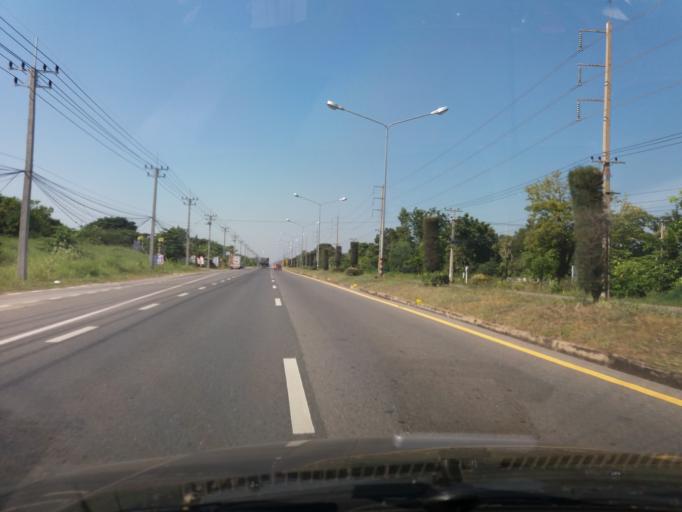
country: TH
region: Chai Nat
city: Chai Nat
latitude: 15.2198
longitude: 100.1138
